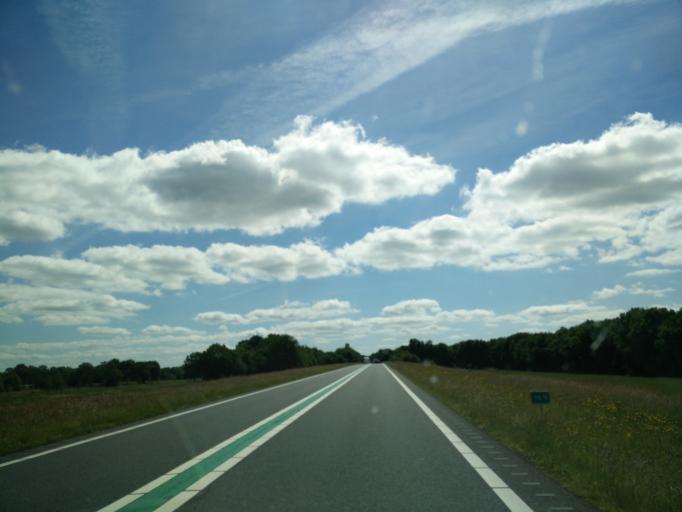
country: NL
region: Drenthe
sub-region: Gemeente Coevorden
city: Sleen
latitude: 52.8075
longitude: 6.6971
